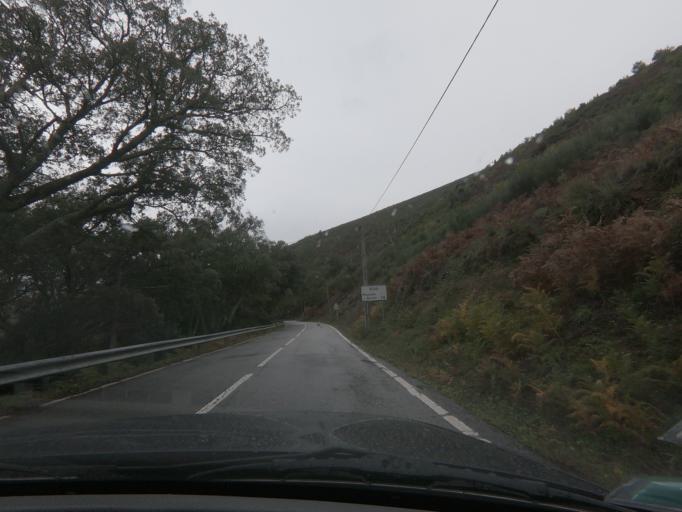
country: PT
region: Vila Real
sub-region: Mondim de Basto
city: Mondim de Basto
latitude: 41.3501
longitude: -7.8844
